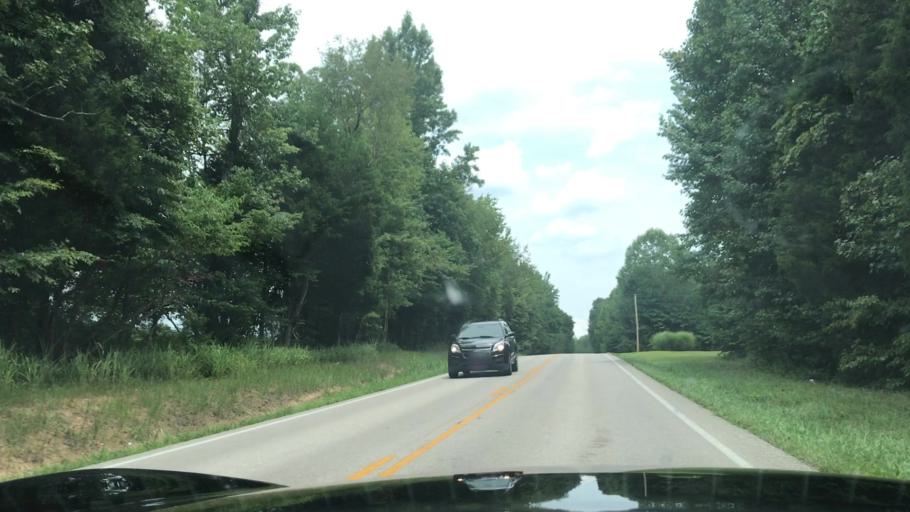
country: US
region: Kentucky
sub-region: Butler County
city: Morgantown
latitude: 37.1789
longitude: -86.7977
